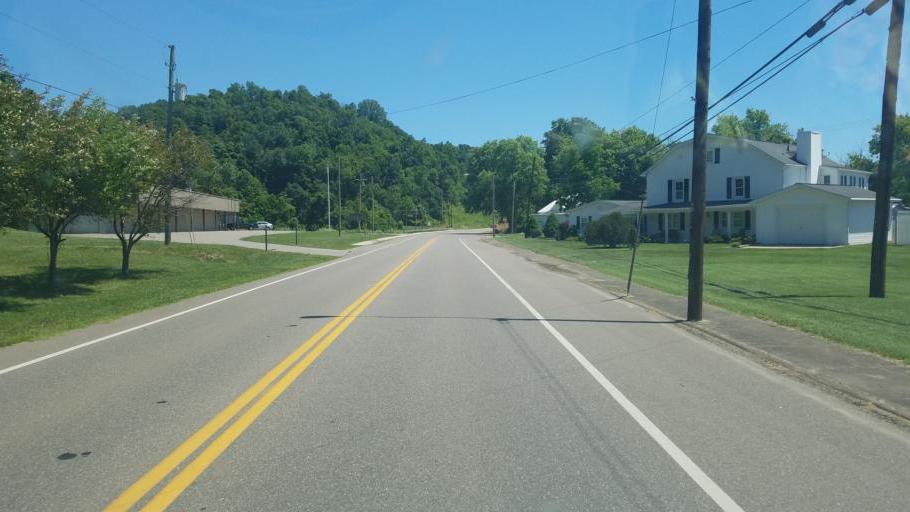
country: US
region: West Virginia
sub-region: Cabell County
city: Lesage
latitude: 38.5915
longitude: -82.2852
